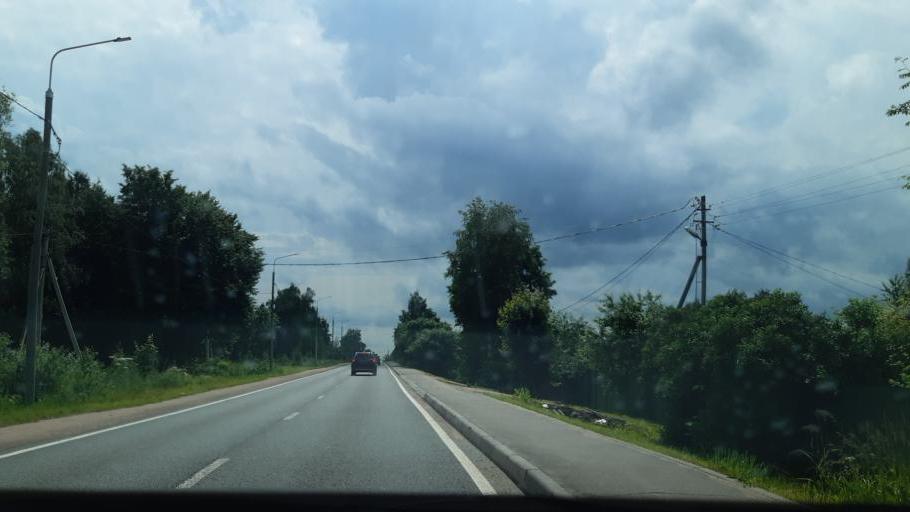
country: RU
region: Moskovskaya
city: Dorokhovo
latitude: 55.5384
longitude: 36.3648
